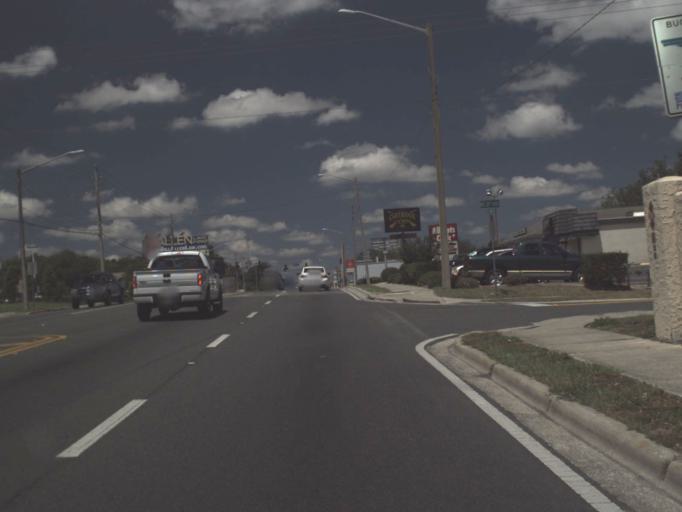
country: US
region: Florida
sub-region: Marion County
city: Ocala
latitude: 29.1871
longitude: -82.1234
